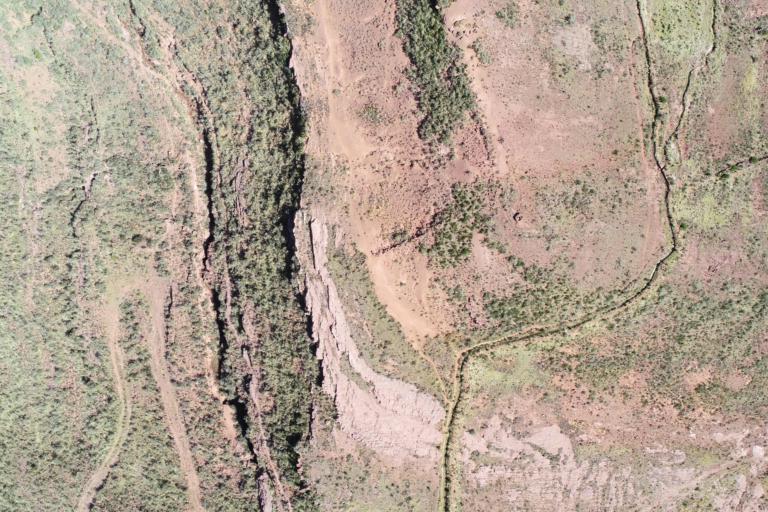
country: BO
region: La Paz
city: Tiahuanaco
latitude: -16.6092
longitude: -68.7684
